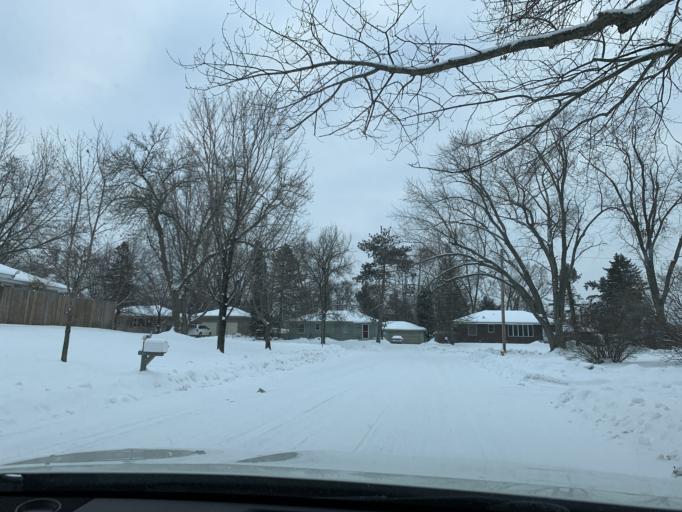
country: US
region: Minnesota
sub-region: Anoka County
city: Coon Rapids
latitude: 45.1720
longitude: -93.2922
